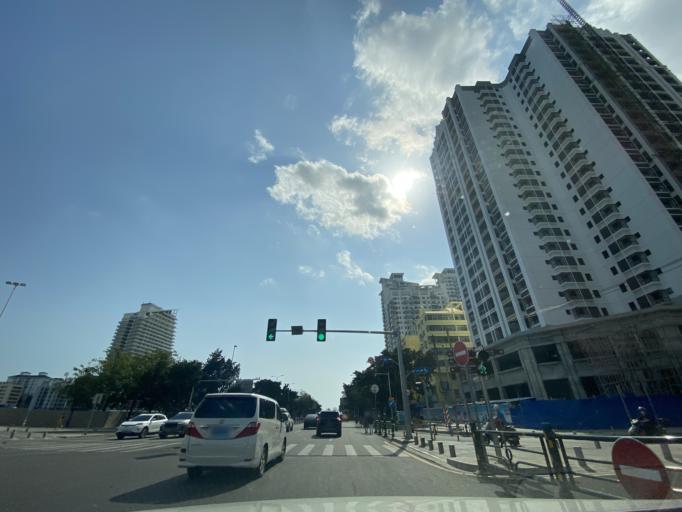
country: CN
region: Hainan
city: Sanya
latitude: 18.2637
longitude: 109.4932
